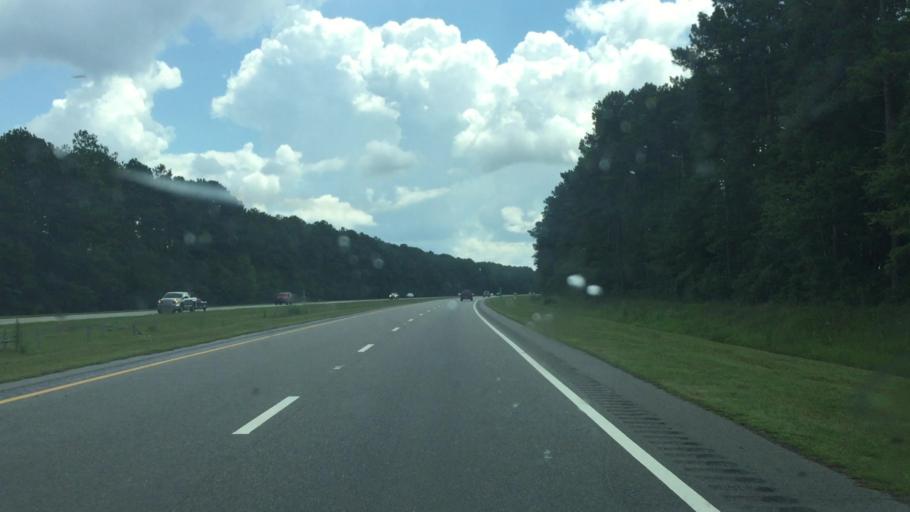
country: US
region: North Carolina
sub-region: Columbus County
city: Chadbourn
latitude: 34.3793
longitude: -78.8527
